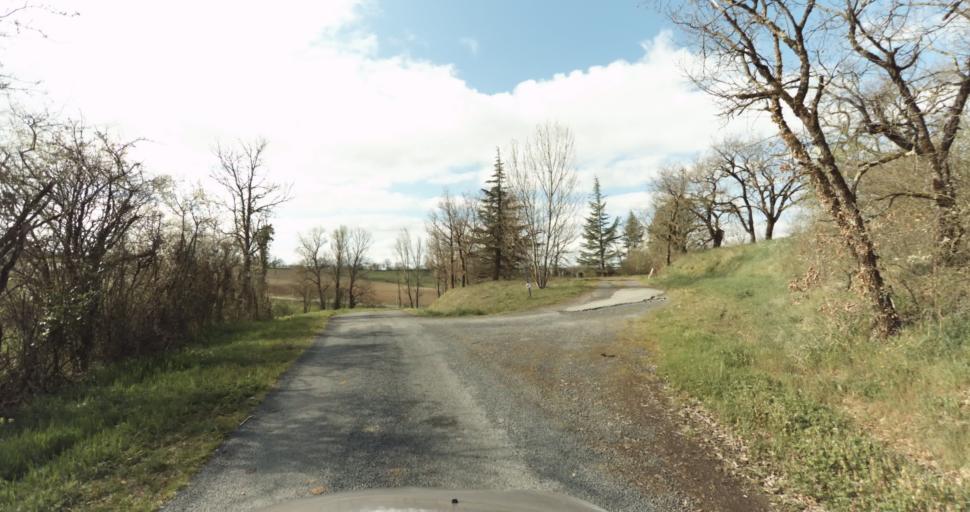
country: FR
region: Midi-Pyrenees
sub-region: Departement du Tarn
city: Frejairolles
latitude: 43.8565
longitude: 2.1961
